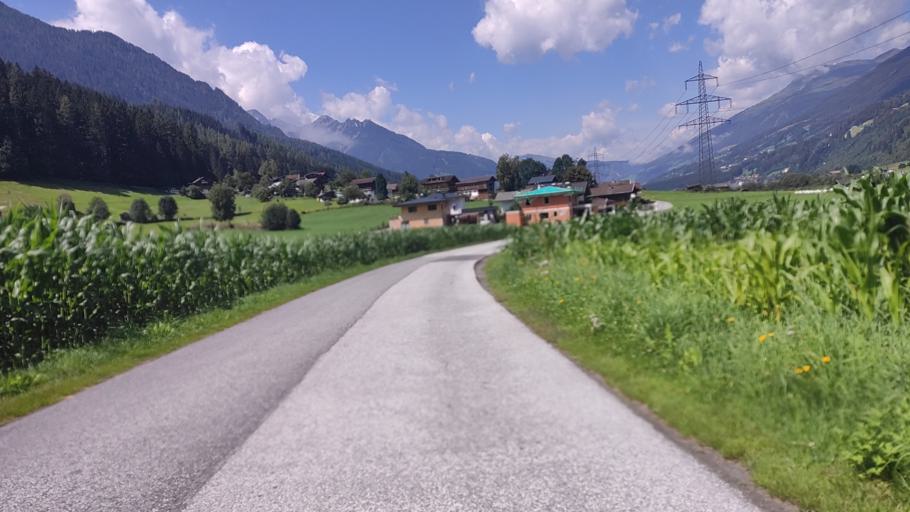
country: AT
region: Salzburg
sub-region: Politischer Bezirk Zell am See
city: Neukirchen am Grossvenediger
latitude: 47.2525
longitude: 12.3136
